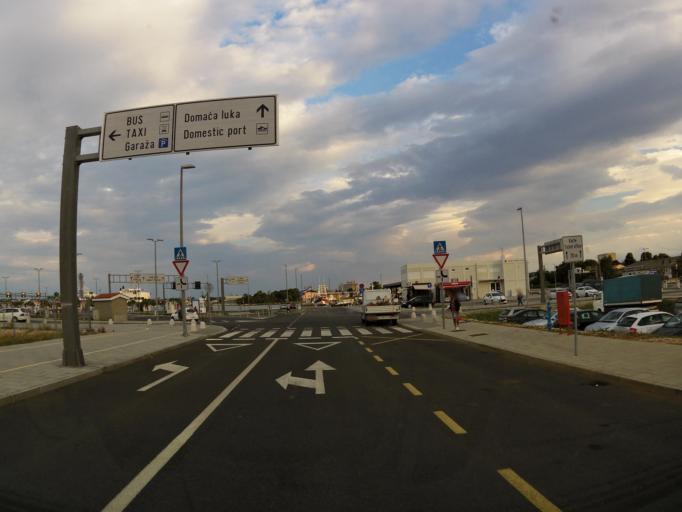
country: HR
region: Zadarska
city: Zadar
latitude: 44.0932
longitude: 15.2601
